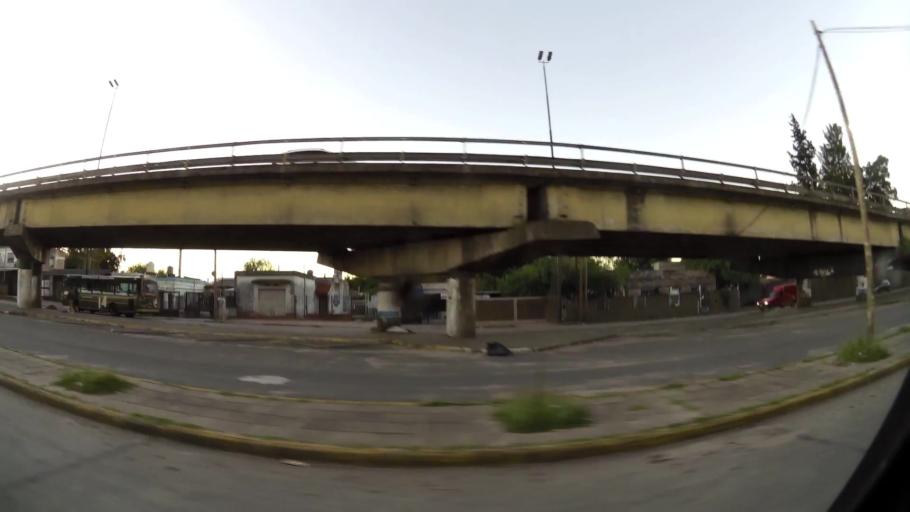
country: AR
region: Buenos Aires
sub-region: Partido de Almirante Brown
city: Adrogue
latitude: -34.8015
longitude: -58.3296
